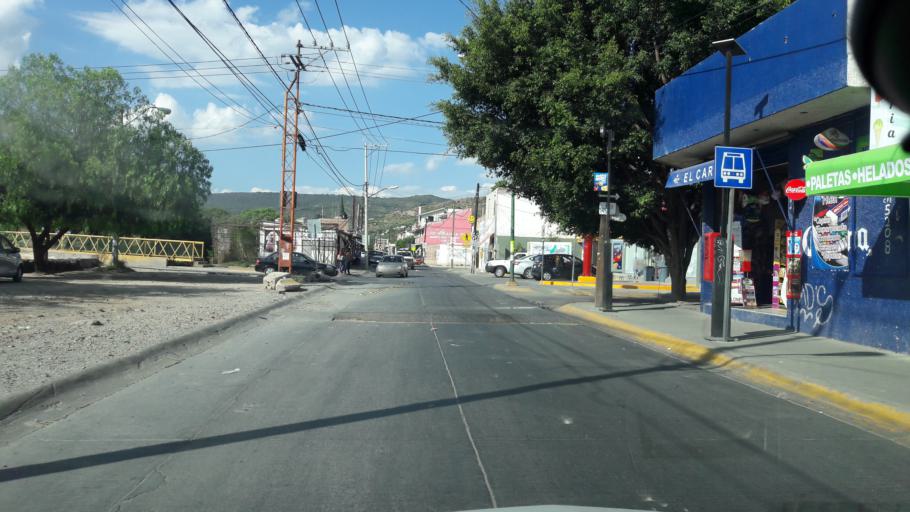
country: MX
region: Guanajuato
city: Leon
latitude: 21.1851
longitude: -101.6667
